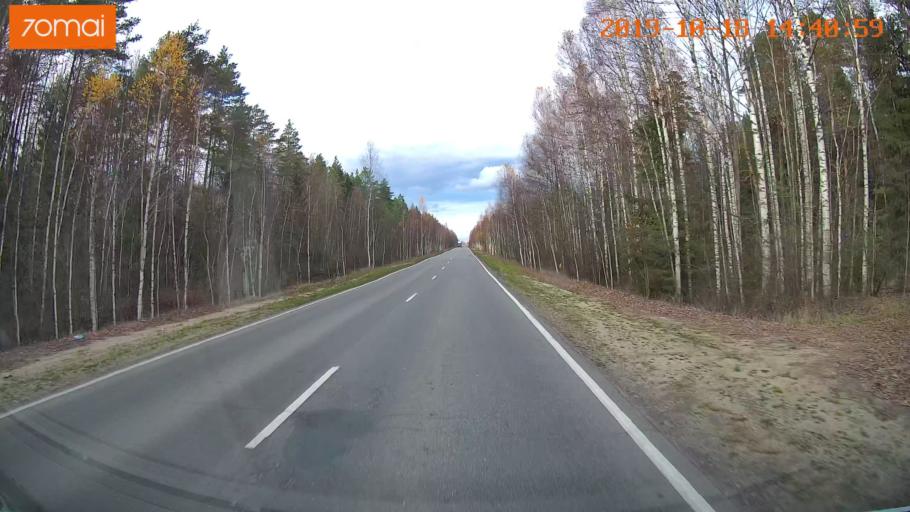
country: RU
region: Vladimir
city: Velikodvorskiy
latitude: 55.2851
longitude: 40.6700
